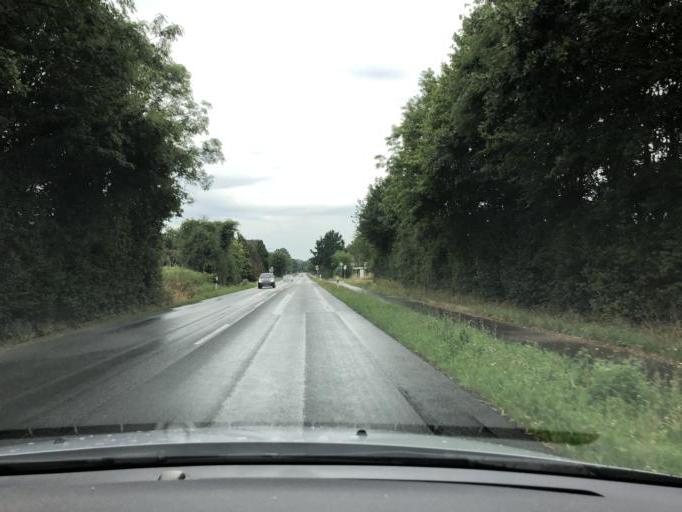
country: DE
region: North Rhine-Westphalia
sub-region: Regierungsbezirk Dusseldorf
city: Schermbeck
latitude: 51.7148
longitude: 6.8734
